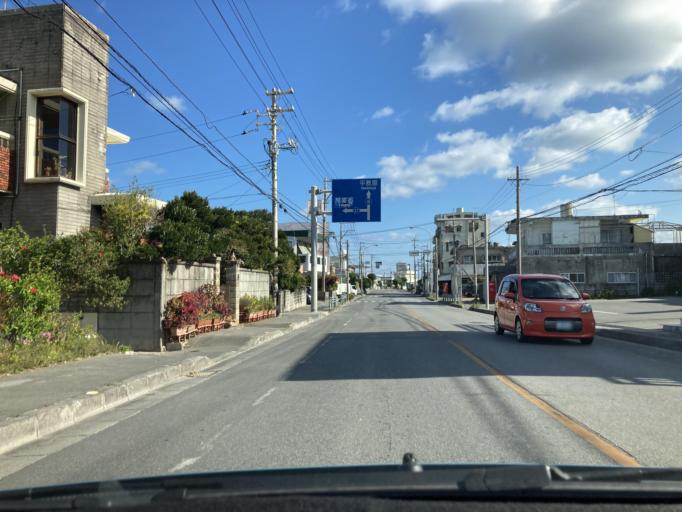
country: JP
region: Okinawa
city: Katsuren-haebaru
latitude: 26.3093
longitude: 127.9112
